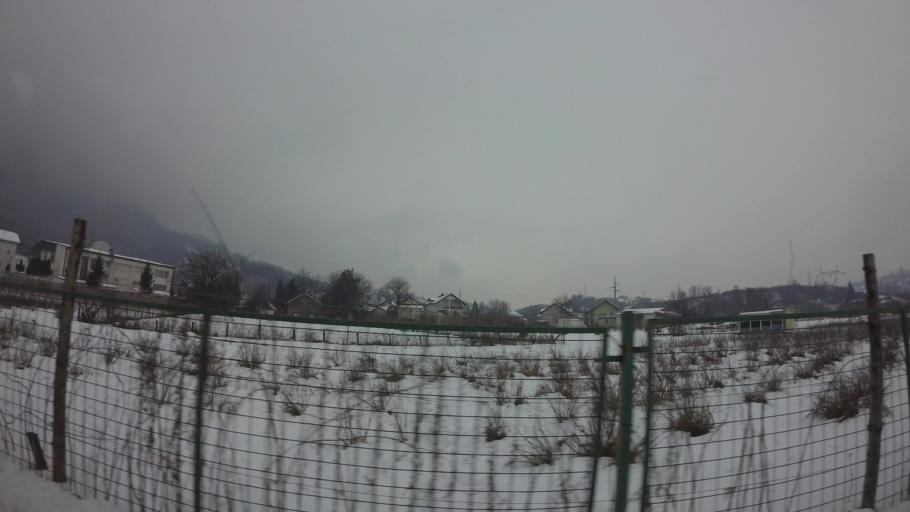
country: BA
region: Federation of Bosnia and Herzegovina
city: Hadzici
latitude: 43.8367
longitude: 18.2695
